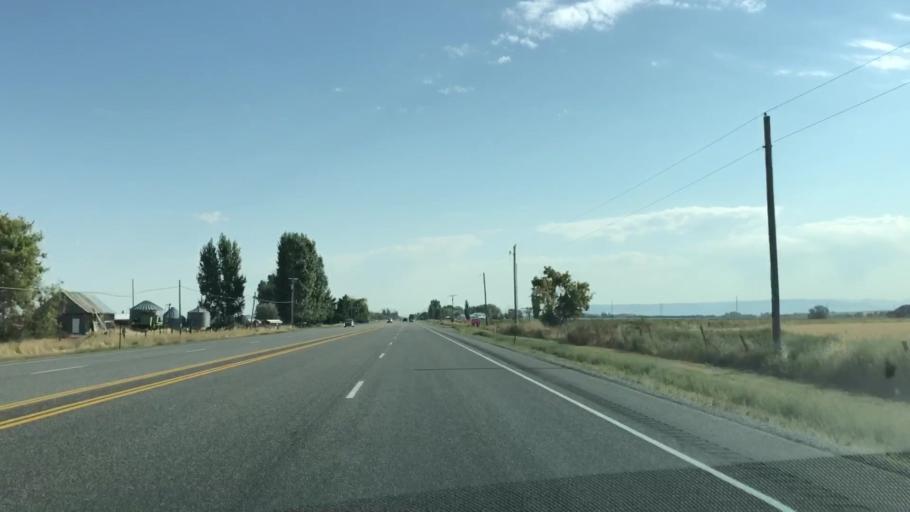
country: US
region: Idaho
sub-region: Bonneville County
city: Iona
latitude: 43.5726
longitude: -111.9119
